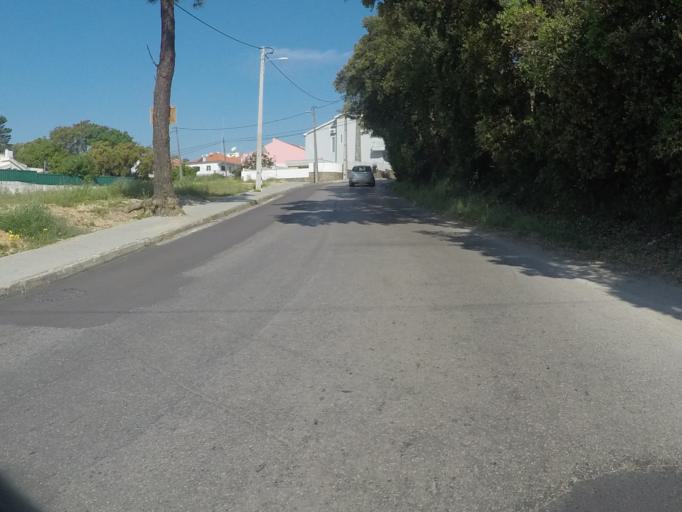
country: PT
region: Setubal
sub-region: Seixal
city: Amora
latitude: 38.6091
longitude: -9.1228
